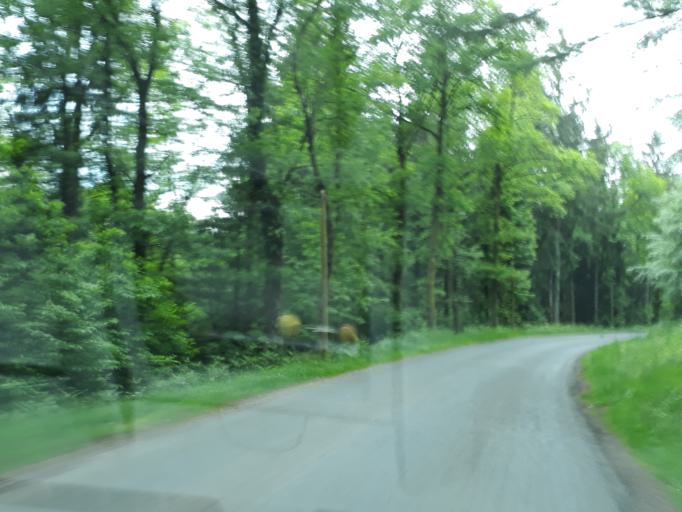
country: FR
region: Limousin
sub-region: Departement de la Haute-Vienne
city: Peyrat-le-Chateau
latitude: 45.8167
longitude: 1.8246
